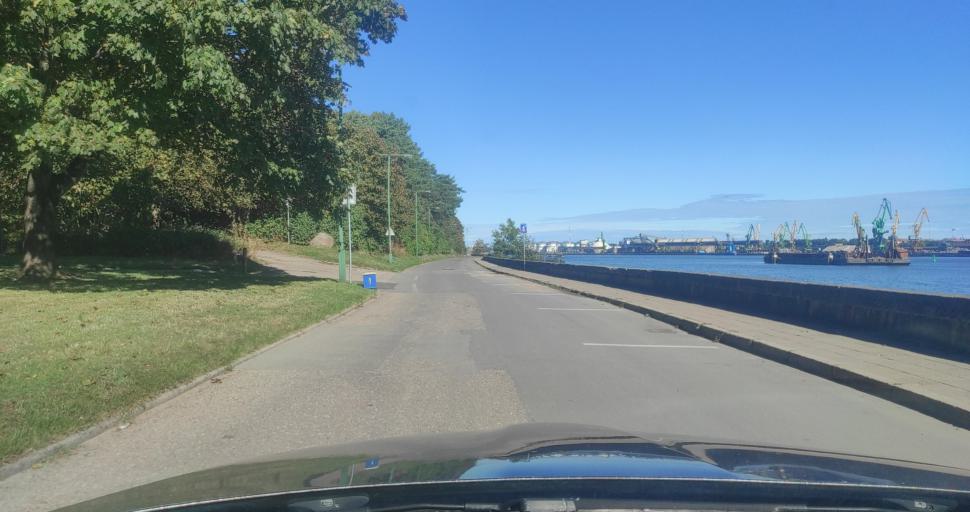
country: LT
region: Klaipedos apskritis
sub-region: Klaipeda
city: Klaipeda
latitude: 55.7083
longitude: 21.1108
